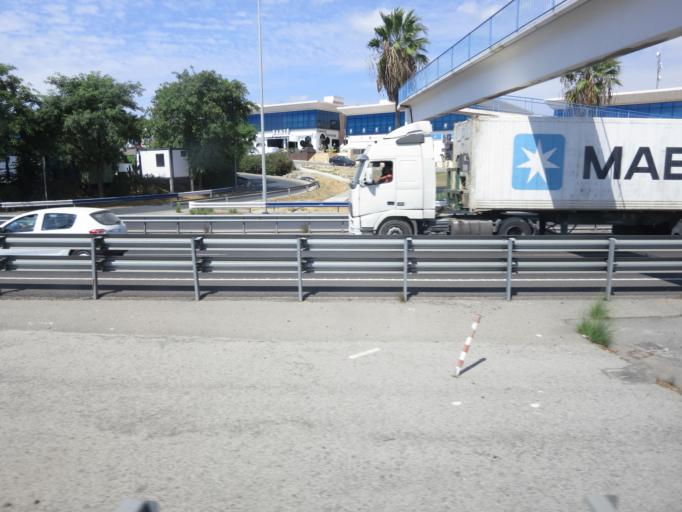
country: ES
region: Andalusia
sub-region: Provincia de Malaga
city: Marbella
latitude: 36.4947
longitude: -4.9504
